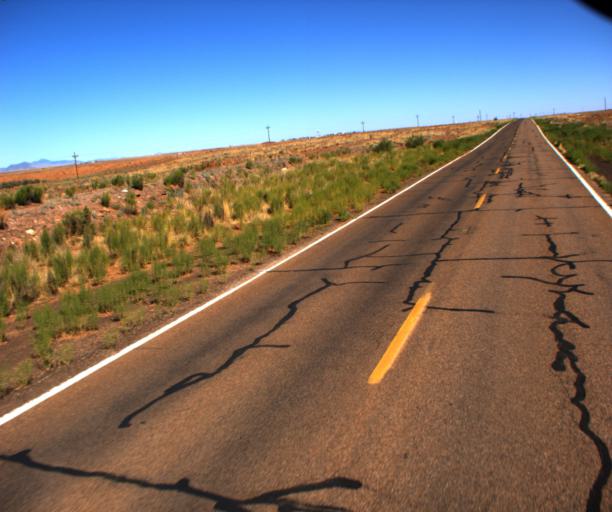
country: US
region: Arizona
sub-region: Coconino County
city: LeChee
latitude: 35.2738
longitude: -110.9774
